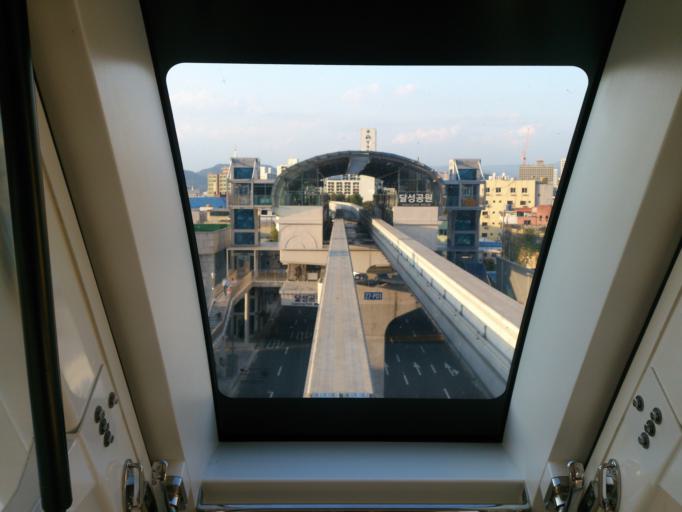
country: KR
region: Daegu
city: Daegu
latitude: 35.8762
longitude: 128.5820
